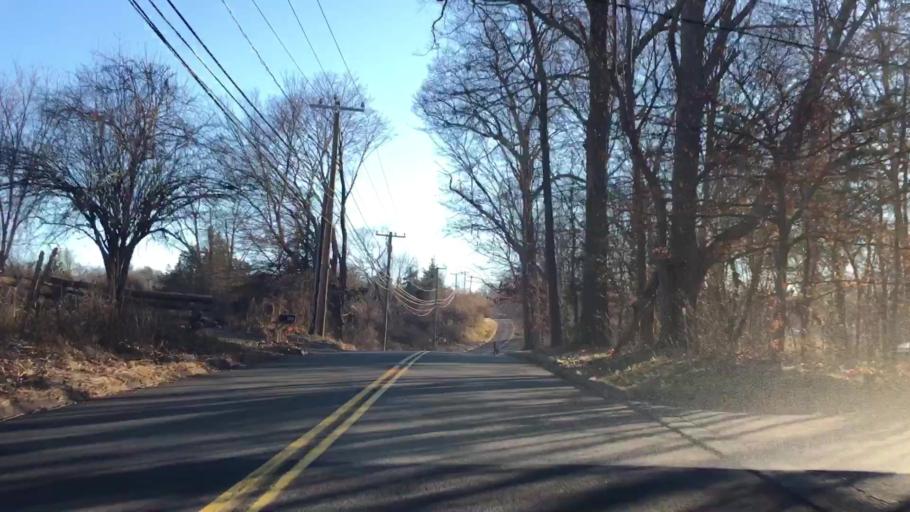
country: US
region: Connecticut
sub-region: New Haven County
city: Meriden
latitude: 41.5474
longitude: -72.8583
